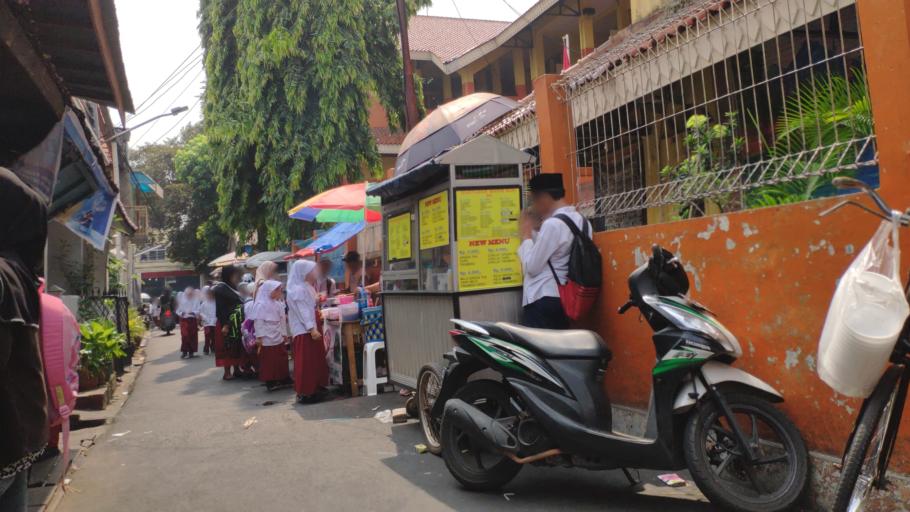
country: ID
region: Banten
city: South Tangerang
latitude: -6.2696
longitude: 106.7745
